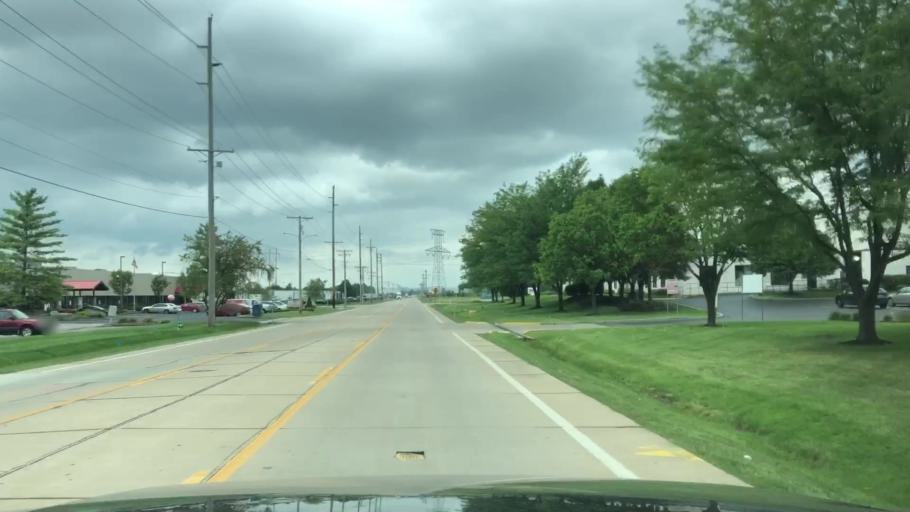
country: US
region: Missouri
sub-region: Saint Charles County
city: Saint Charles
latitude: 38.8221
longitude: -90.5023
